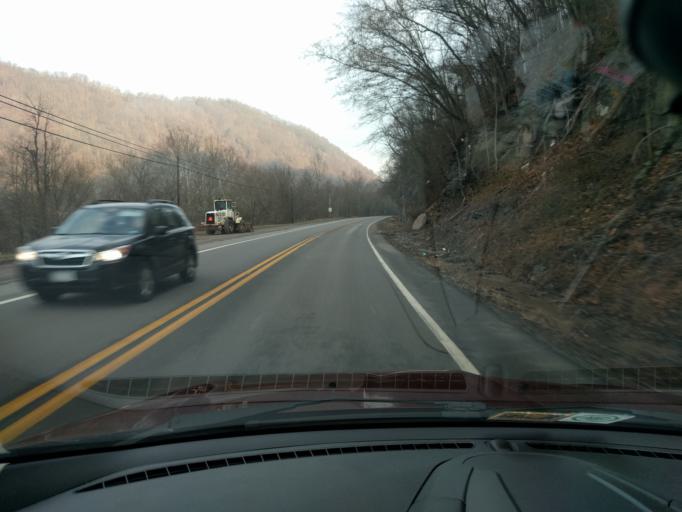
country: US
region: West Virginia
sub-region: Kanawha County
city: Montgomery
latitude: 38.1625
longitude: -81.3009
